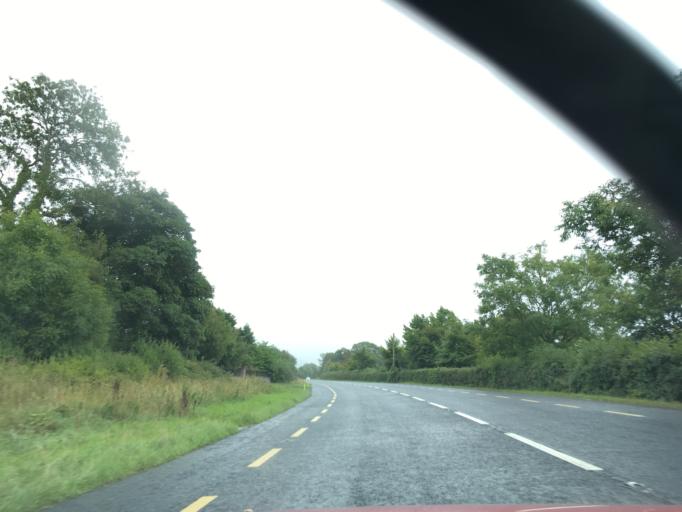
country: IE
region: Munster
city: Carrick-on-Suir
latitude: 52.3606
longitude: -7.4979
